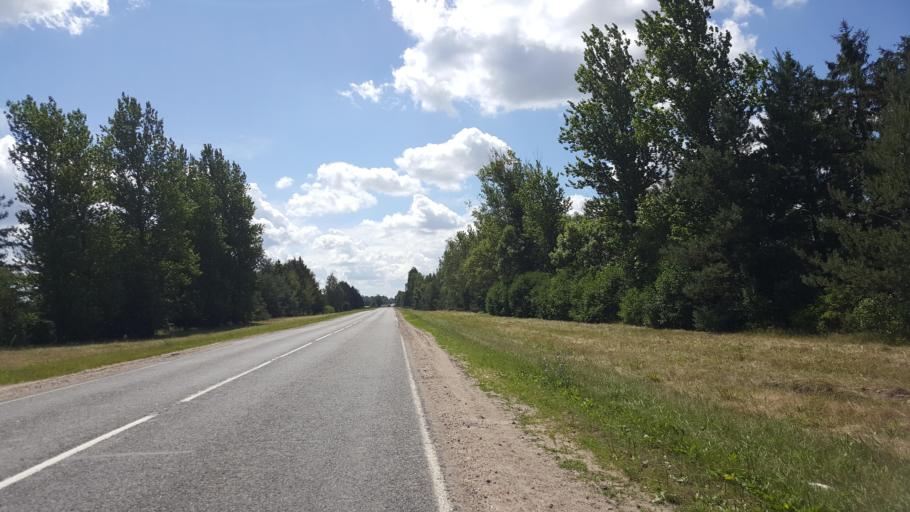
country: BY
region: Brest
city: Kamyanyets
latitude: 52.3544
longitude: 23.8967
